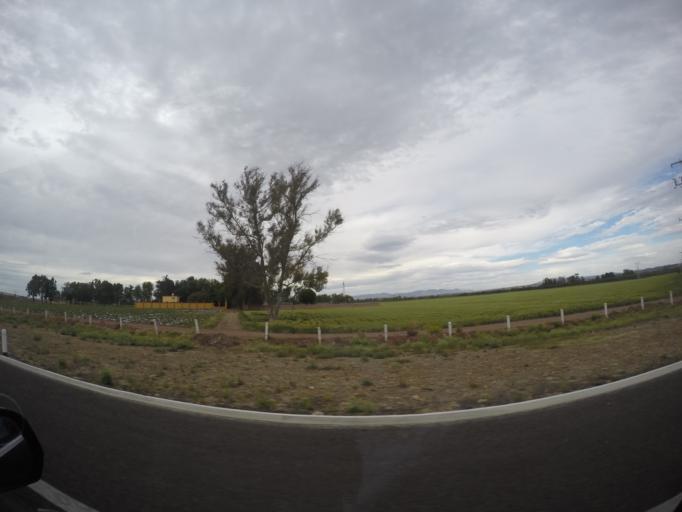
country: MX
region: Guanajuato
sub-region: Irapuato
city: Serrano
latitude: 20.7980
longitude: -101.4276
